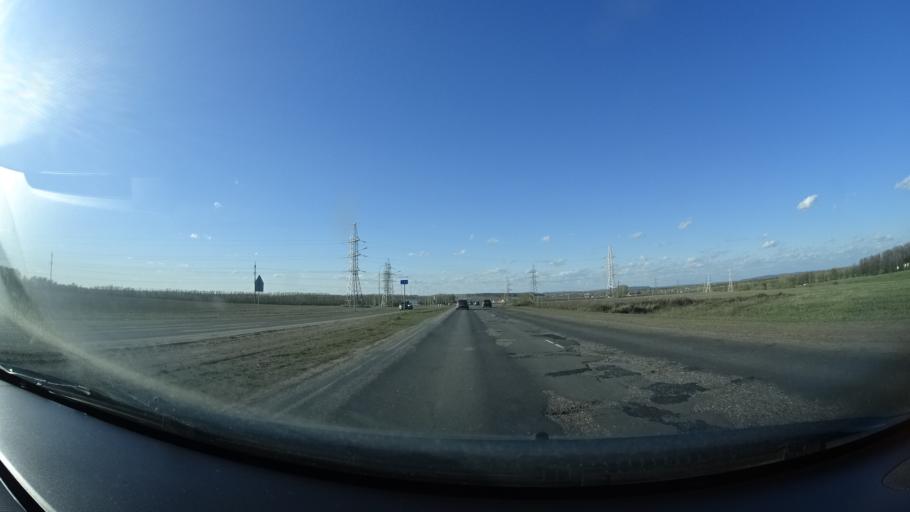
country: RU
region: Bashkortostan
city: Kabakovo
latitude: 54.4786
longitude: 55.9103
